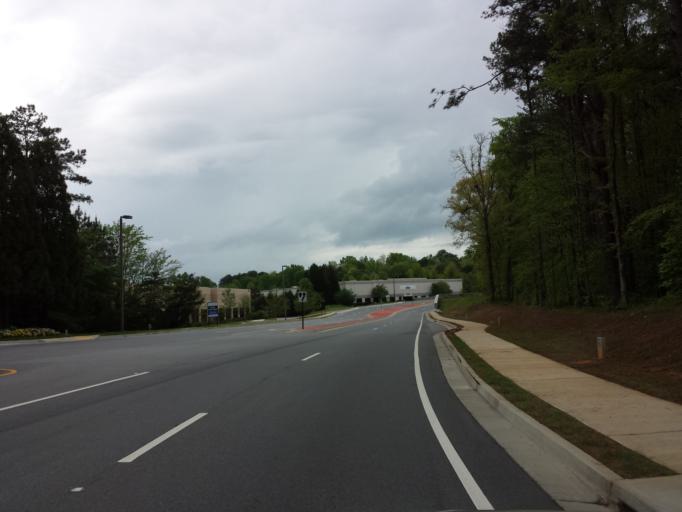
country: US
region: Georgia
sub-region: Cobb County
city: Kennesaw
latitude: 34.0240
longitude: -84.5807
